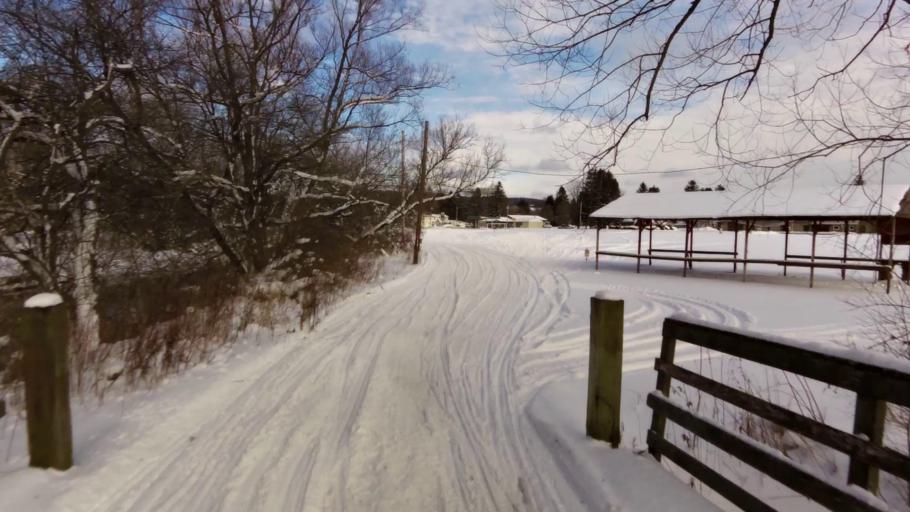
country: US
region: New York
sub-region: Cattaraugus County
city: Franklinville
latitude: 42.3434
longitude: -78.4579
